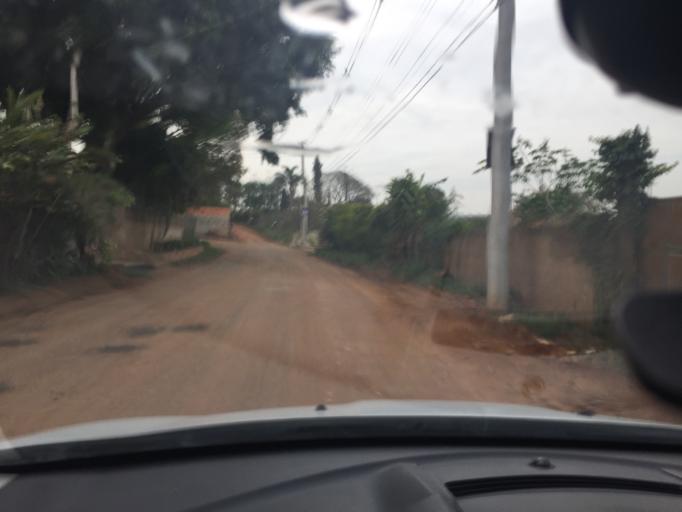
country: BR
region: Sao Paulo
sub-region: Campo Limpo Paulista
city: Campo Limpo Paulista
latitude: -23.1582
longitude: -46.7882
